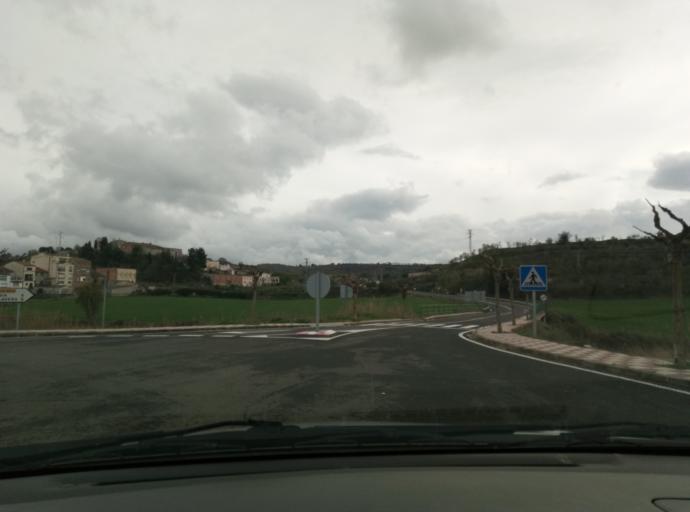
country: ES
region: Catalonia
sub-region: Provincia de Lleida
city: Cervera
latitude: 41.6290
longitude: 1.3406
